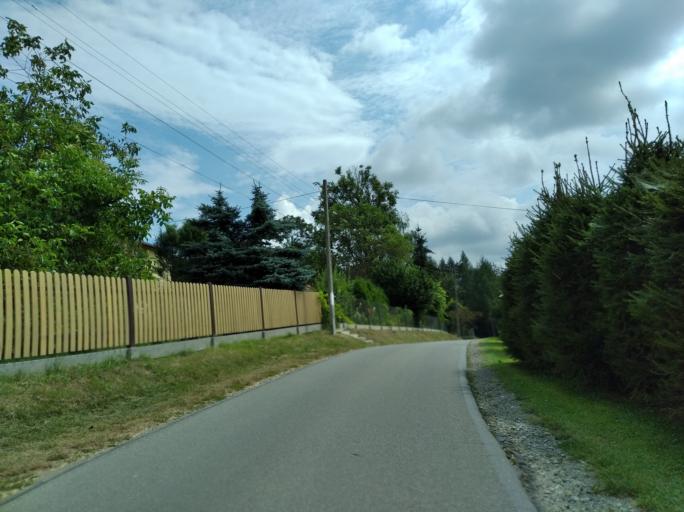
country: PL
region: Subcarpathian Voivodeship
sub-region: Powiat krosnienski
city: Wojaszowka
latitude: 49.7870
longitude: 21.6951
